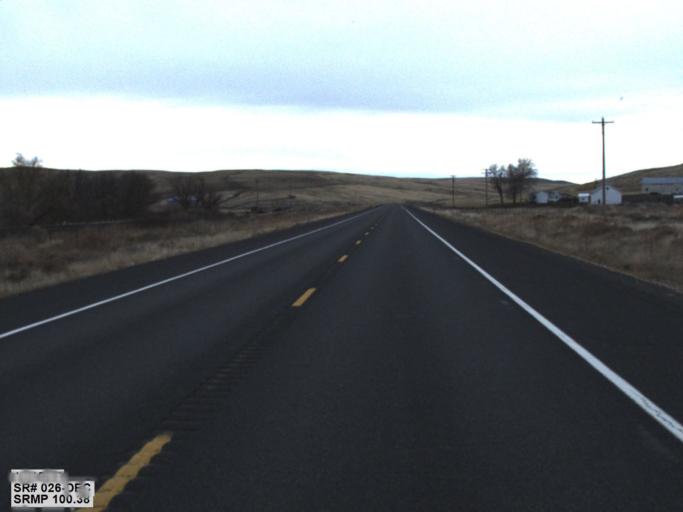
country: US
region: Washington
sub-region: Columbia County
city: Dayton
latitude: 46.7661
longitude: -117.9760
